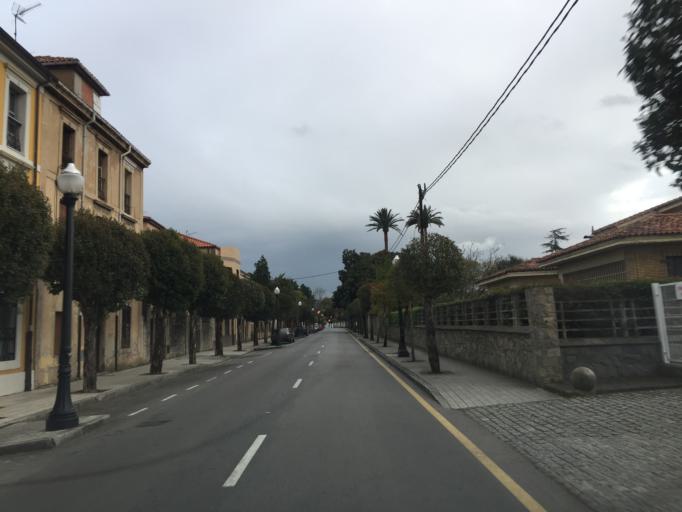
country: ES
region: Asturias
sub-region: Province of Asturias
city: Gijon
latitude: 43.5331
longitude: -5.6313
